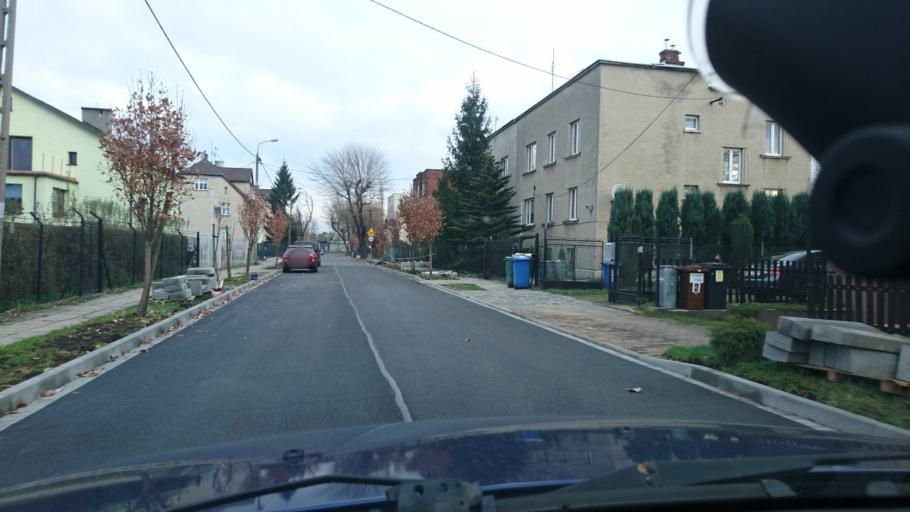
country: PL
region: Silesian Voivodeship
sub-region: Bielsko-Biala
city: Bielsko-Biala
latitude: 49.8297
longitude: 19.0573
